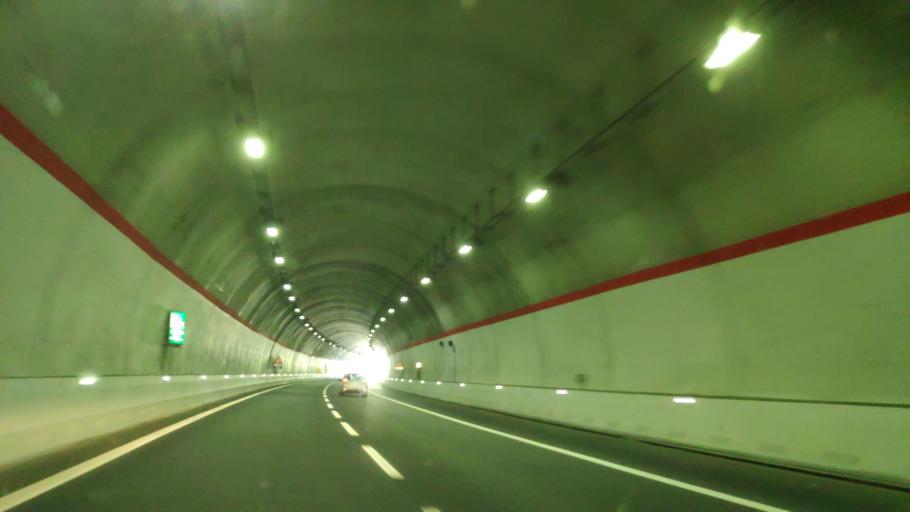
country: IT
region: Basilicate
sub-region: Provincia di Potenza
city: Lagonegro
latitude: 40.1129
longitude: 15.7882
